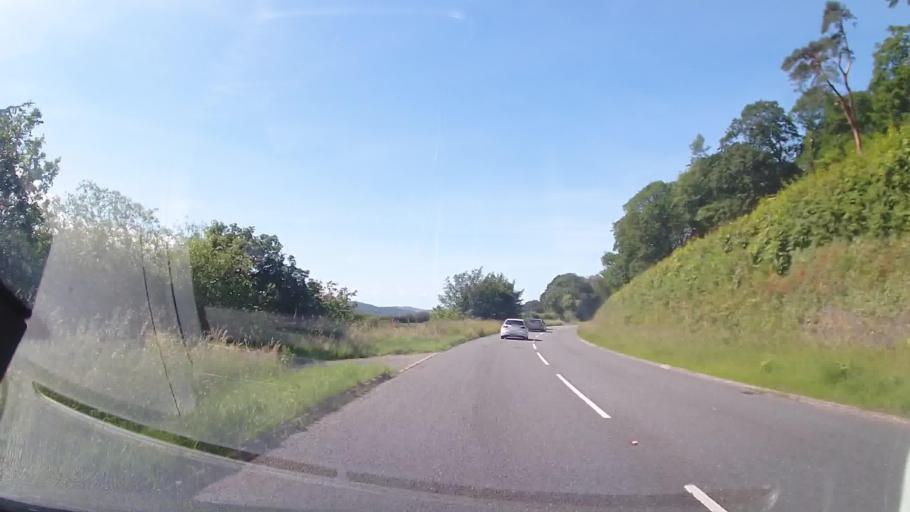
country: GB
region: Wales
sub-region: Sir Powys
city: Machynlleth
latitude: 52.5650
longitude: -3.9571
